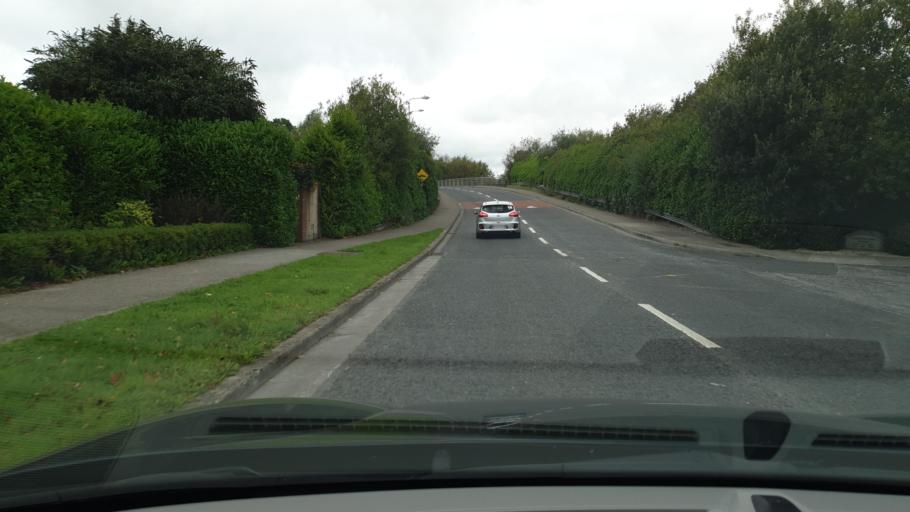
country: IE
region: Leinster
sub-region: Kildare
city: Naas
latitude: 53.2154
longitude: -6.6779
